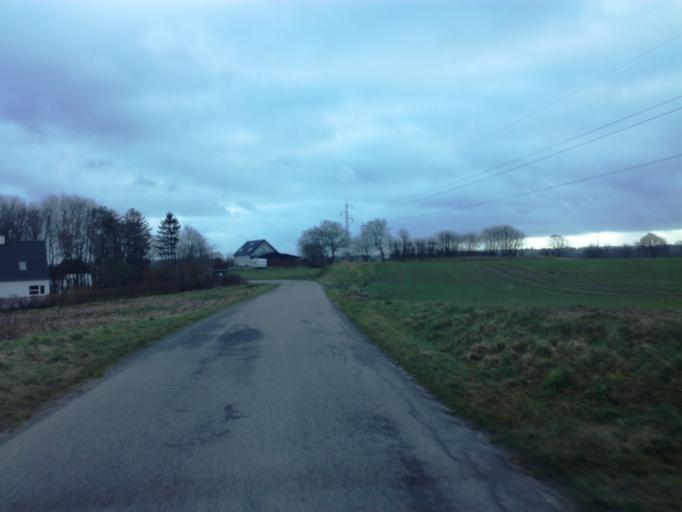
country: DK
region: South Denmark
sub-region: Vejle Kommune
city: Brejning
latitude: 55.6246
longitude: 9.7205
